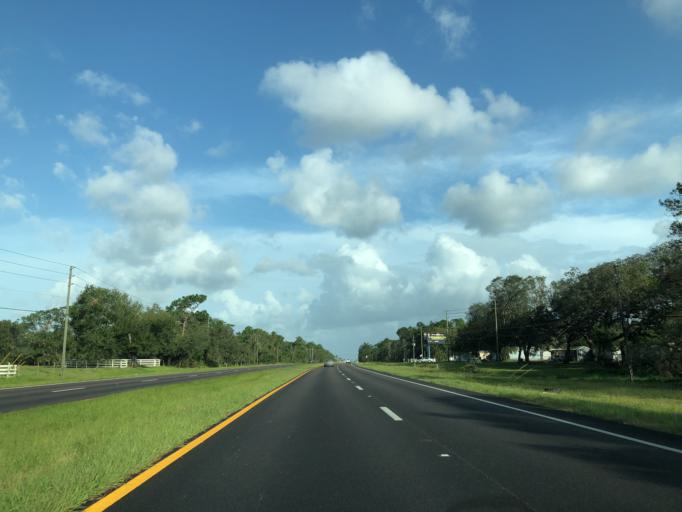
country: US
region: Florida
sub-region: Orange County
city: Bithlo
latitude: 28.5643
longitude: -81.1418
